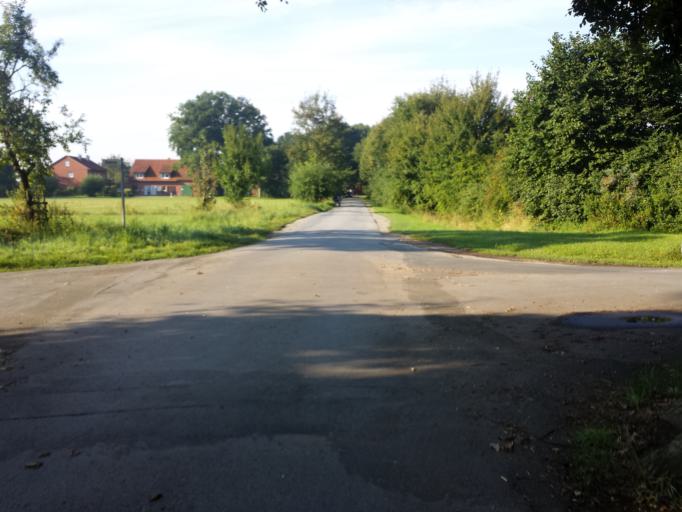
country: DE
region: North Rhine-Westphalia
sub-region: Regierungsbezirk Detmold
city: Harsewinkel
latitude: 51.9532
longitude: 8.2631
